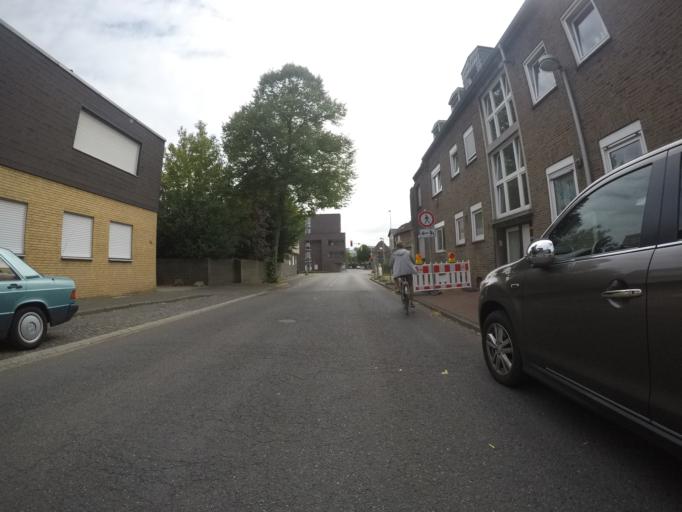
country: DE
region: North Rhine-Westphalia
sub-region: Regierungsbezirk Dusseldorf
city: Bocholt
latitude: 51.8409
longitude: 6.6070
